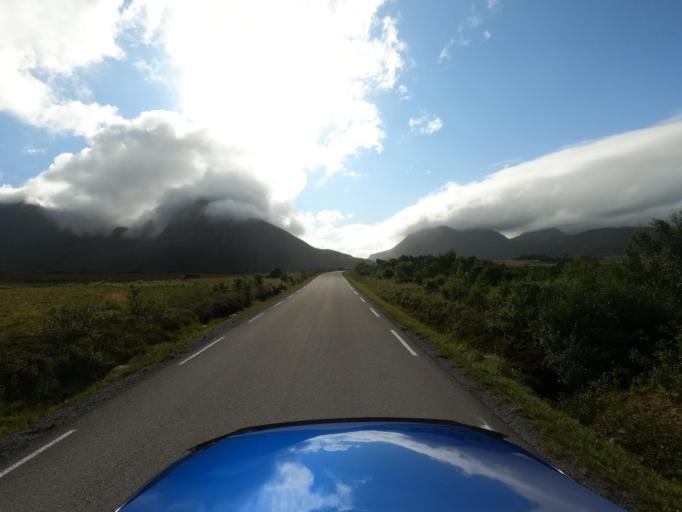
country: NO
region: Nordland
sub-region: Vagan
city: Kabelvag
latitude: 68.2946
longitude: 14.1679
